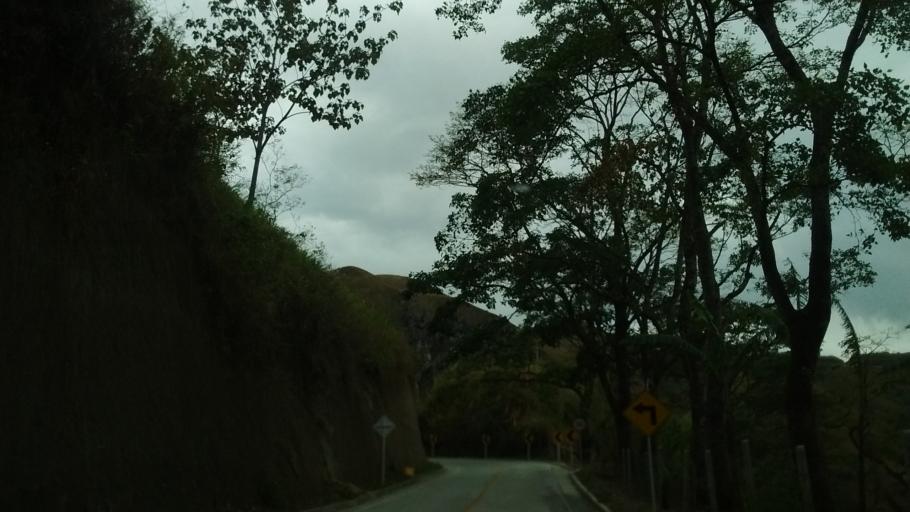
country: CO
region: Cauca
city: La Sierra
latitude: 2.1512
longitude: -76.7724
